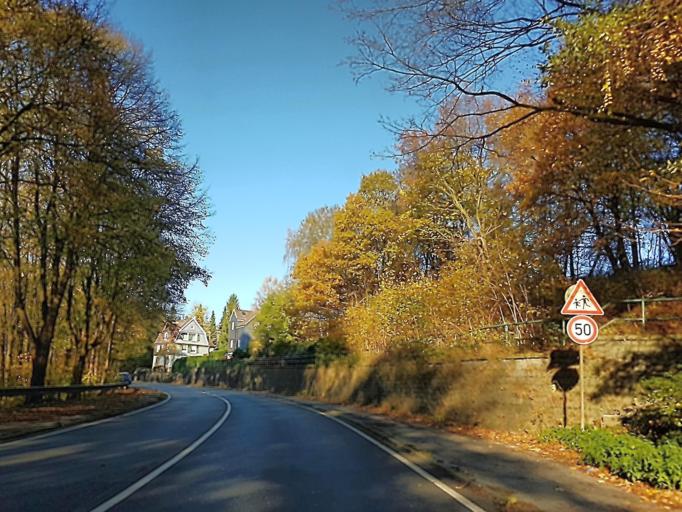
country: DE
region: North Rhine-Westphalia
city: Huckeswagen
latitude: 51.1896
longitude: 7.2792
